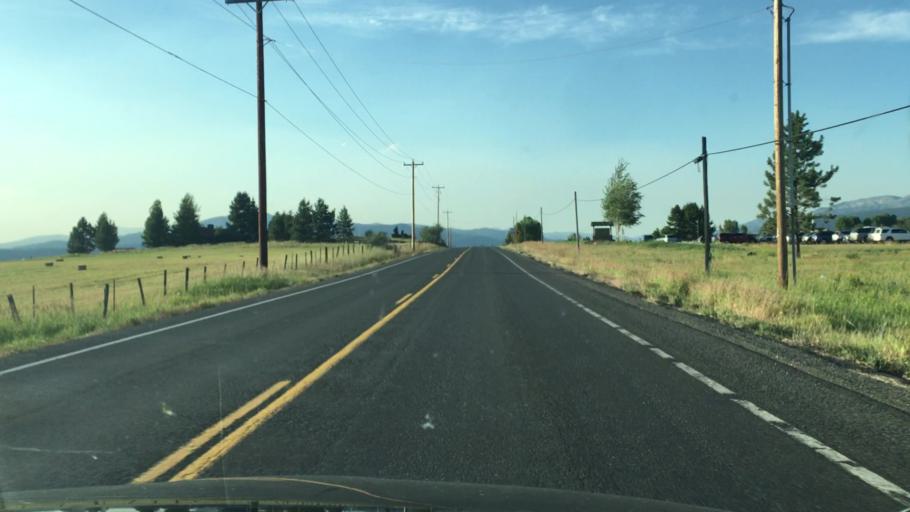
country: US
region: Idaho
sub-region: Valley County
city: McCall
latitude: 44.8785
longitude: -116.0907
